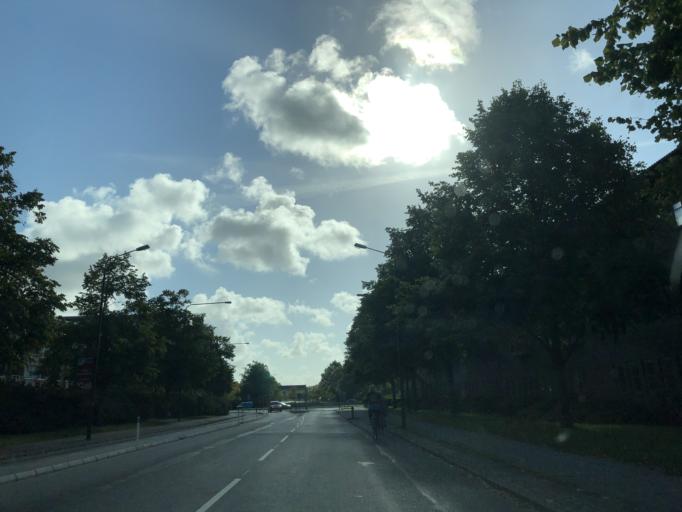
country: SE
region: Skane
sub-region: Malmo
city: Malmoe
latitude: 55.5838
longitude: 12.9777
